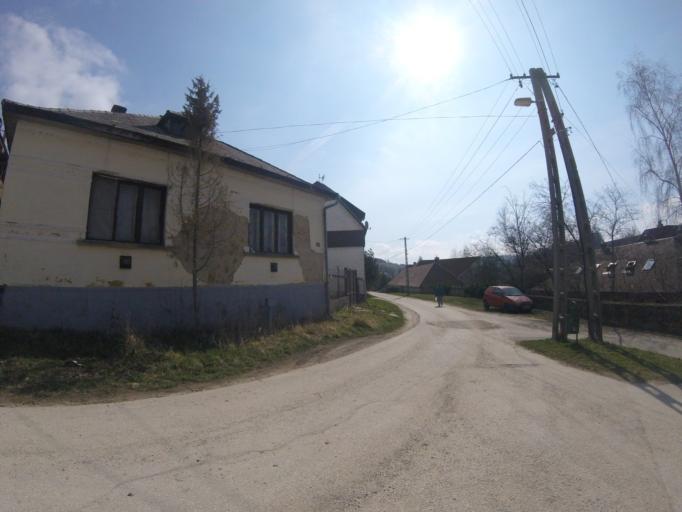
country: HU
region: Komarom-Esztergom
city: Nyergesujfalu
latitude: 47.7272
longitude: 18.5593
